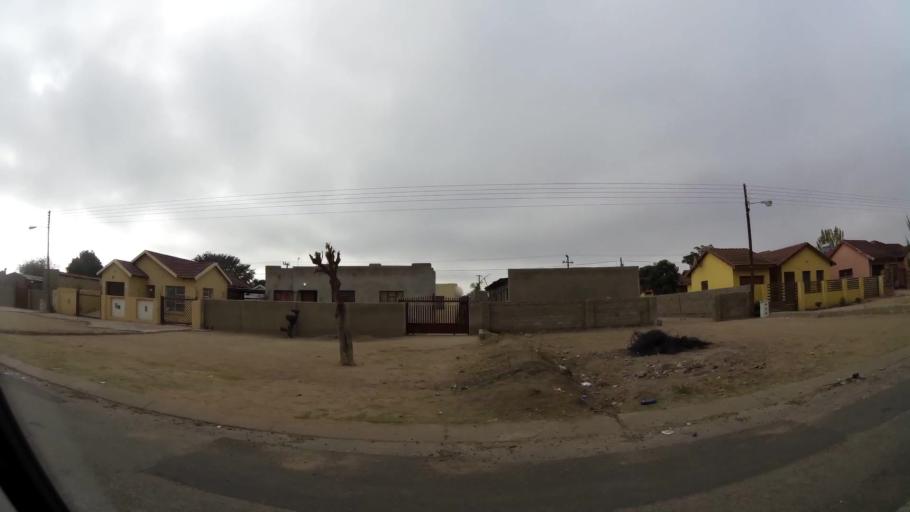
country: ZA
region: Limpopo
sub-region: Capricorn District Municipality
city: Polokwane
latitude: -23.8346
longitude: 29.3824
